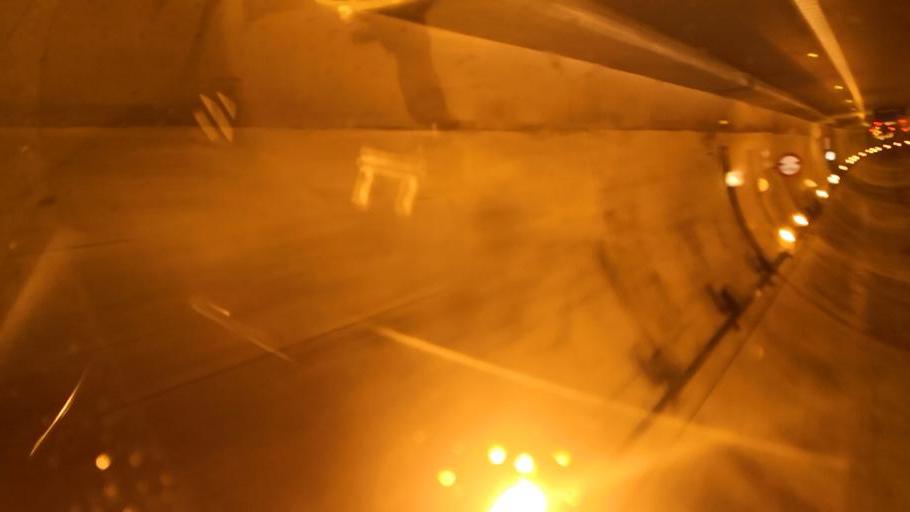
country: ES
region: Galicia
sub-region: Provincia de Pontevedra
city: Vigo
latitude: 42.2405
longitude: -8.6670
